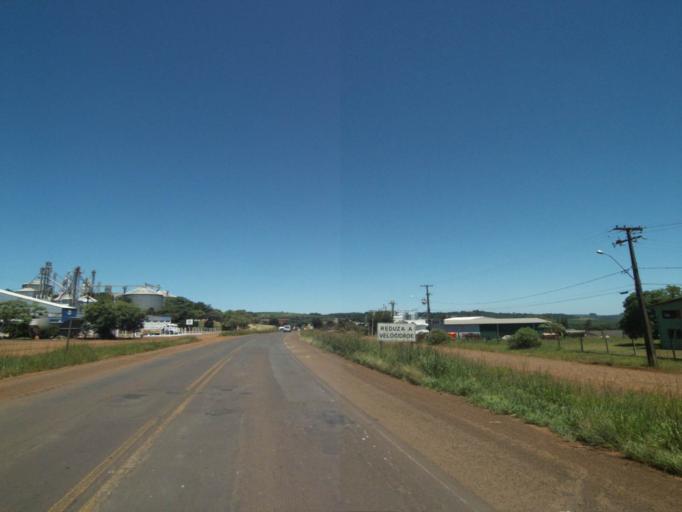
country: BR
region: Parana
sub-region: Pato Branco
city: Pato Branco
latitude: -26.2601
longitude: -52.7687
